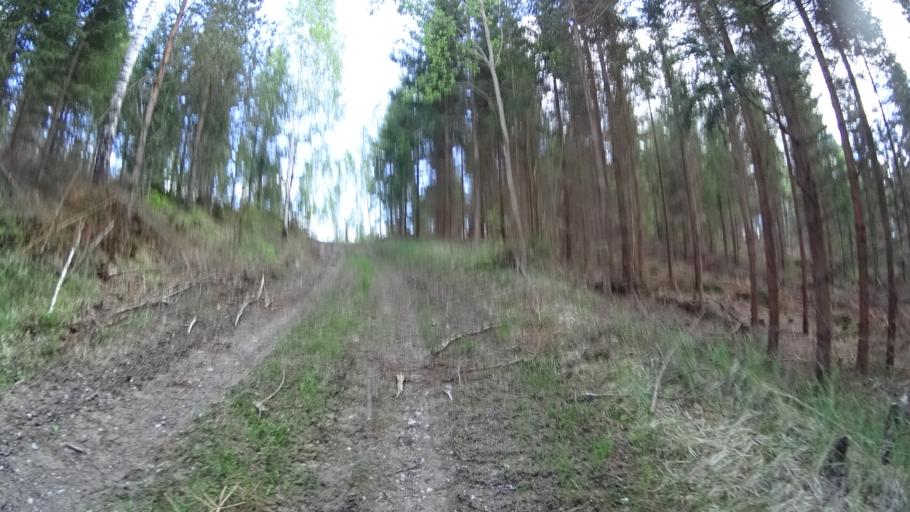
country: FI
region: Uusimaa
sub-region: Raaseporin
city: Pohja
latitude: 60.1633
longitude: 23.6068
